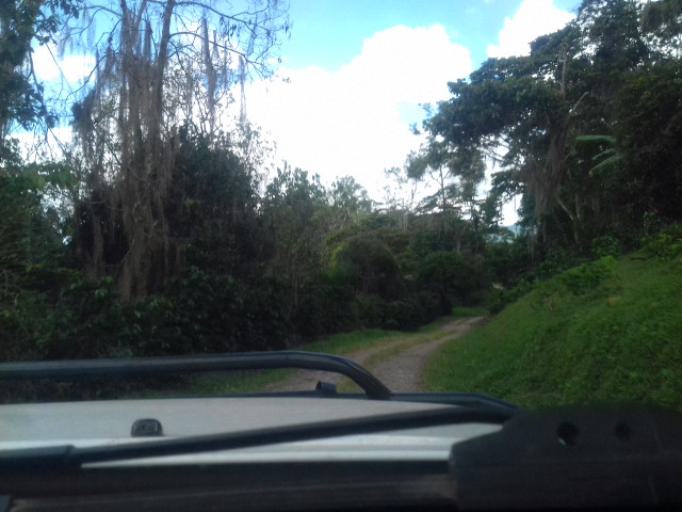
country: NI
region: Atlantico Norte (RAAN)
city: Waslala
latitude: 13.2071
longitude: -85.5830
